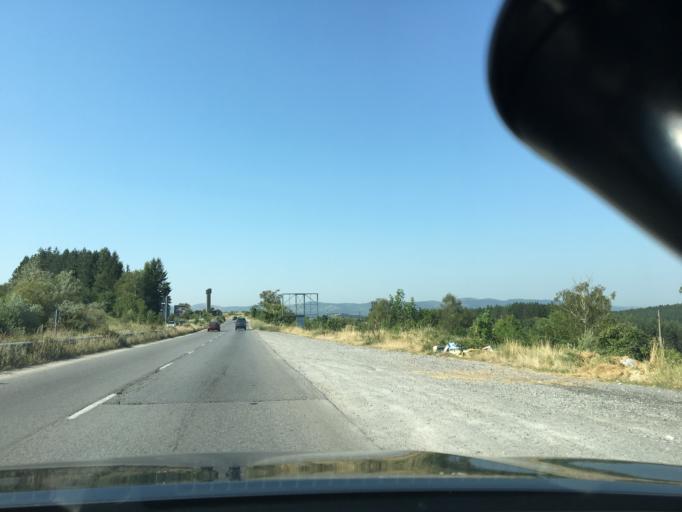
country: BG
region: Sofiya
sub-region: Obshtina Bozhurishte
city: Bozhurishte
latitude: 42.6179
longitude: 23.1769
